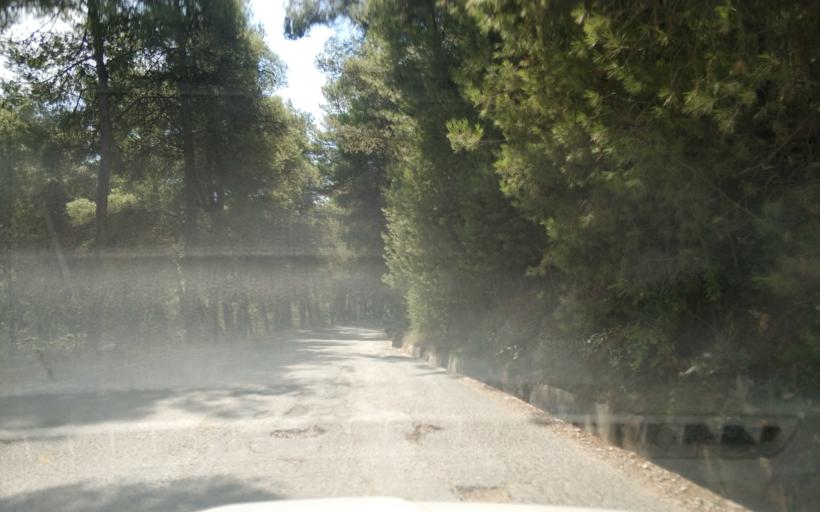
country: AL
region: Durres
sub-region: Rrethi i Krujes
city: Kruje
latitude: 41.4967
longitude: 19.7754
